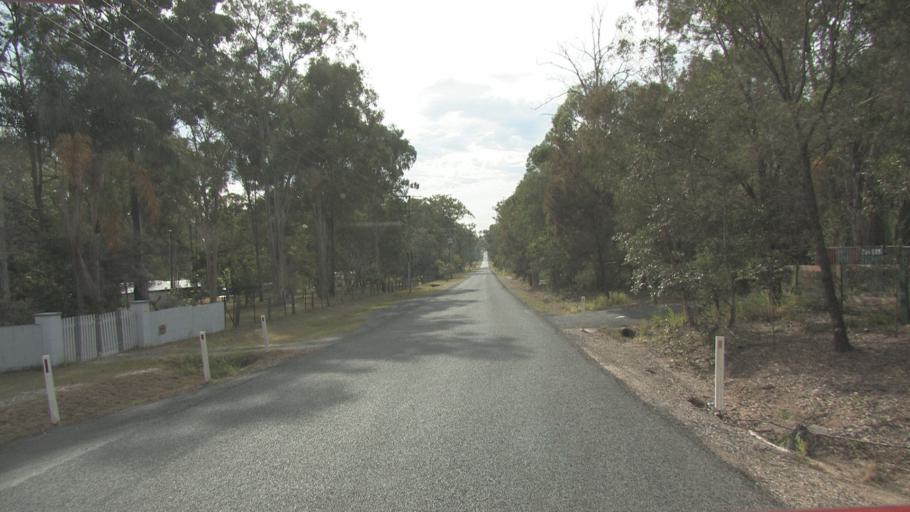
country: AU
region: Queensland
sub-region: Logan
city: Chambers Flat
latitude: -27.7941
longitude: 153.1216
